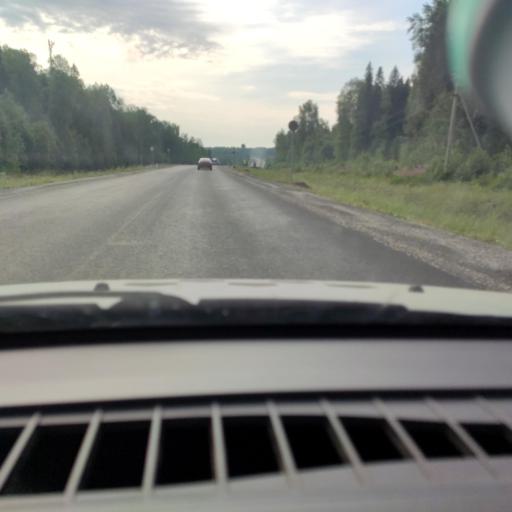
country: RU
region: Perm
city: Siva
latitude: 58.5517
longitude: 53.9041
